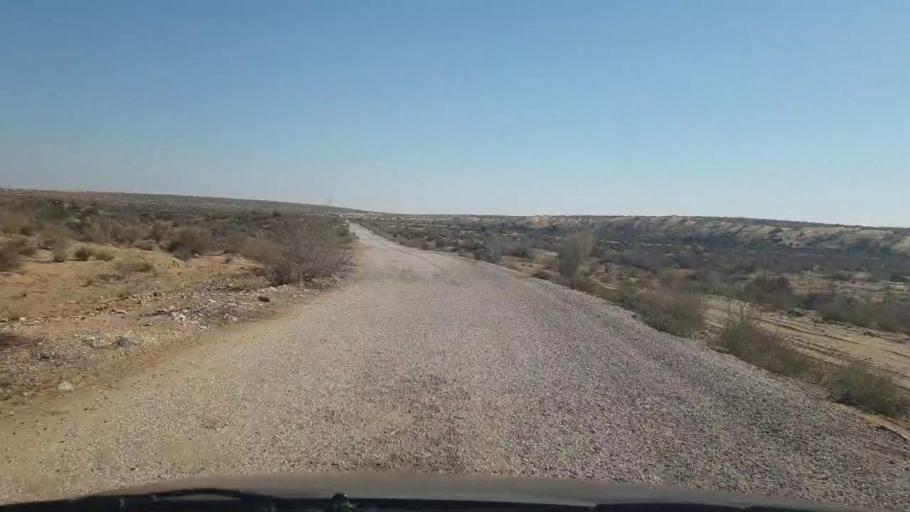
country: PK
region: Sindh
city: Bozdar
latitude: 27.0222
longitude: 68.7168
